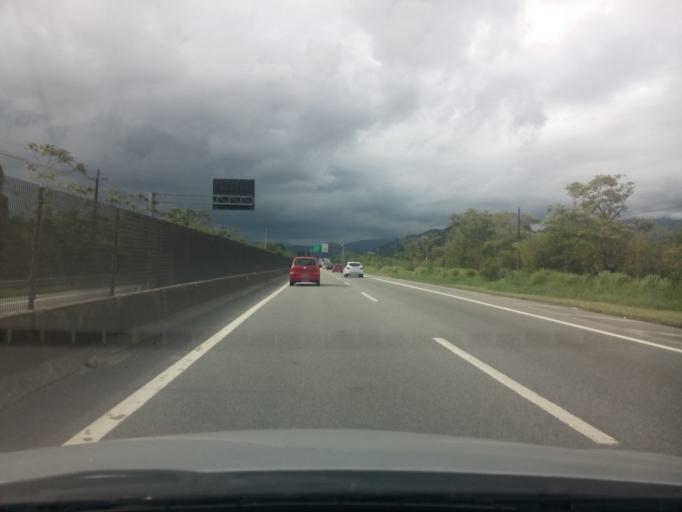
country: BR
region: Sao Paulo
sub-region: Santos
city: Santos
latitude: -23.9336
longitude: -46.2831
